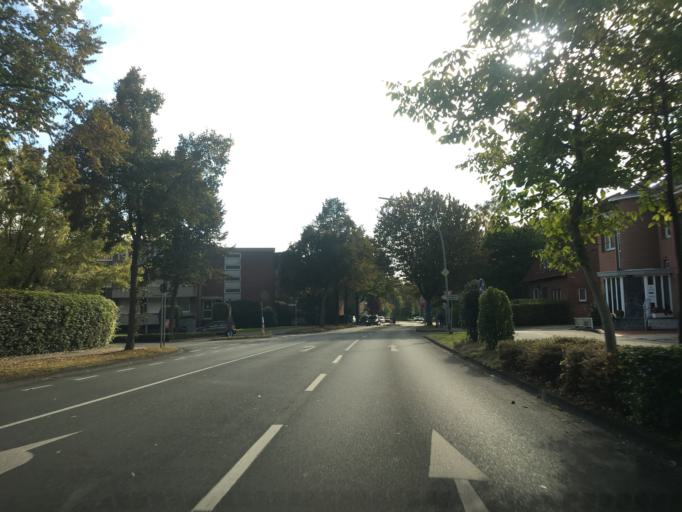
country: DE
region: North Rhine-Westphalia
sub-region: Regierungsbezirk Munster
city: Muenster
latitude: 51.9532
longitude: 7.5319
